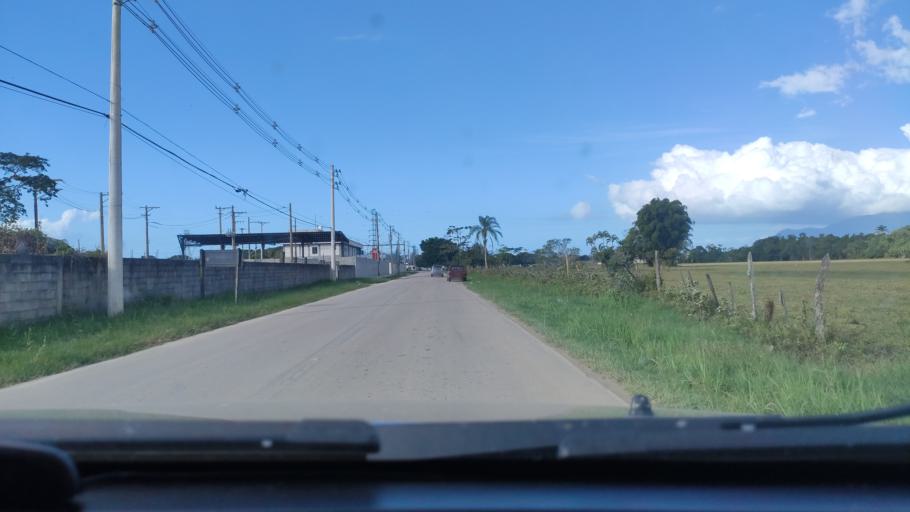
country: BR
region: Sao Paulo
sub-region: Sao Sebastiao
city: Sao Sebastiao
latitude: -23.6927
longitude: -45.4485
